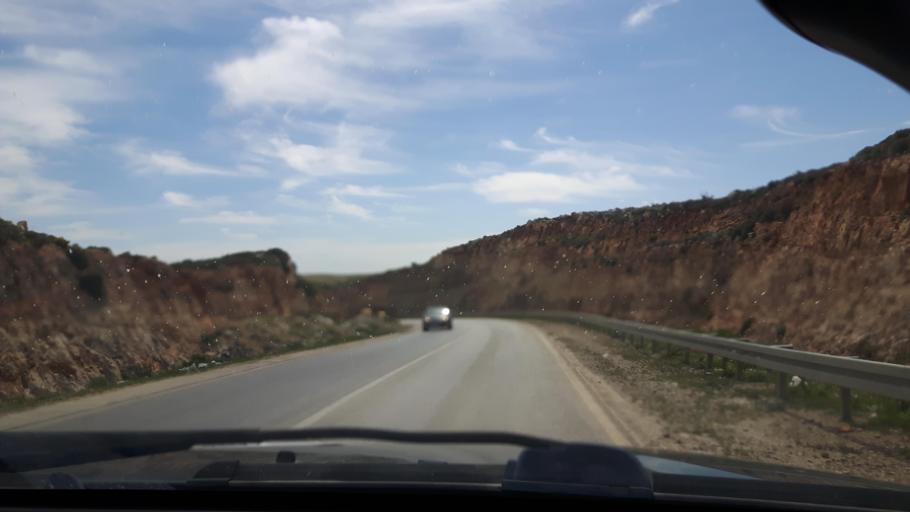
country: PS
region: West Bank
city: Qalandiya
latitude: 31.8667
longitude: 35.2007
